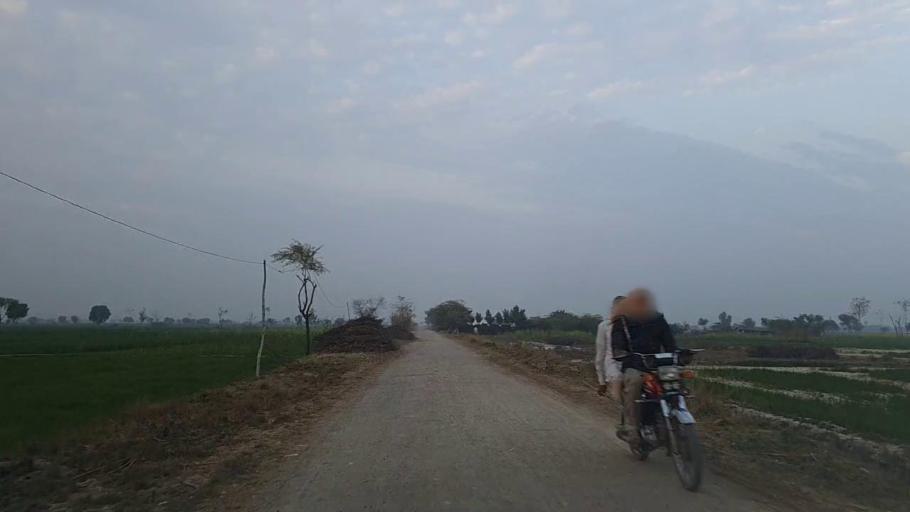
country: PK
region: Sindh
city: Jam Sahib
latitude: 26.3041
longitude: 68.5936
